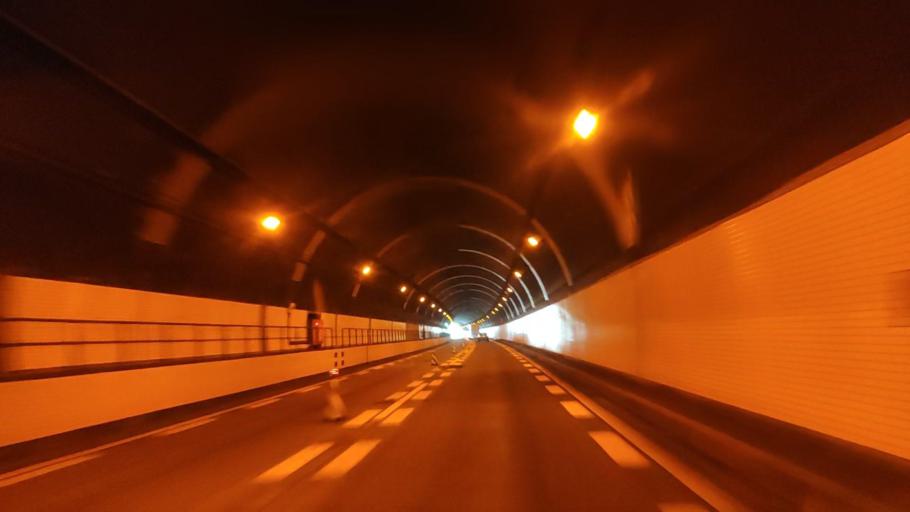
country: JP
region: Niigata
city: Joetsu
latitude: 37.1091
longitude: 138.0466
